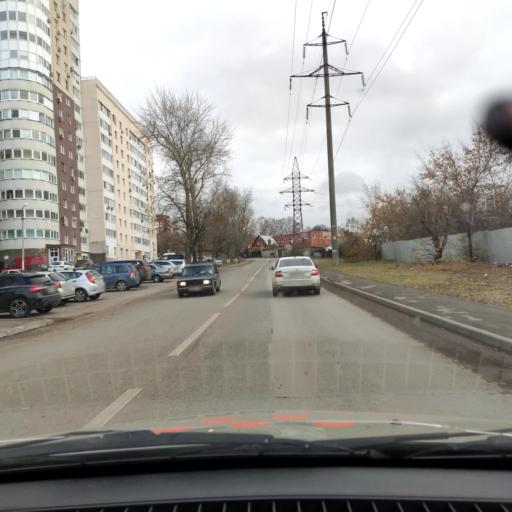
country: RU
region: Bashkortostan
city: Ufa
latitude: 54.7083
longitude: 55.9915
